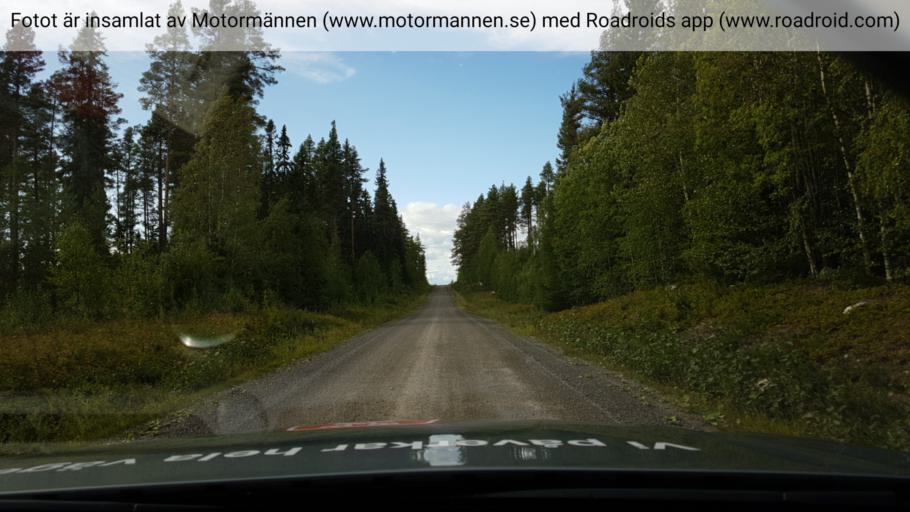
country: SE
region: Jaemtland
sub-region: OEstersunds Kommun
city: Lit
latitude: 63.2890
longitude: 15.3553
